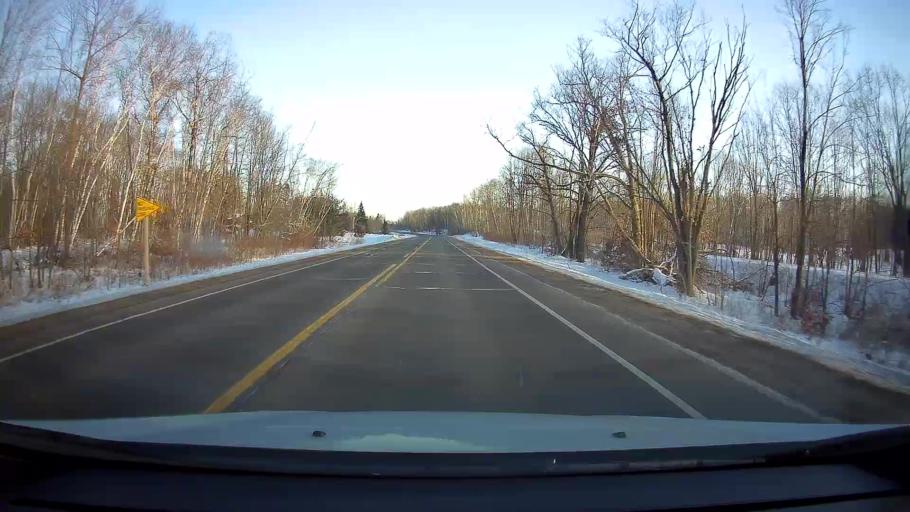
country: US
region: Wisconsin
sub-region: Barron County
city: Turtle Lake
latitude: 45.4175
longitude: -92.1316
